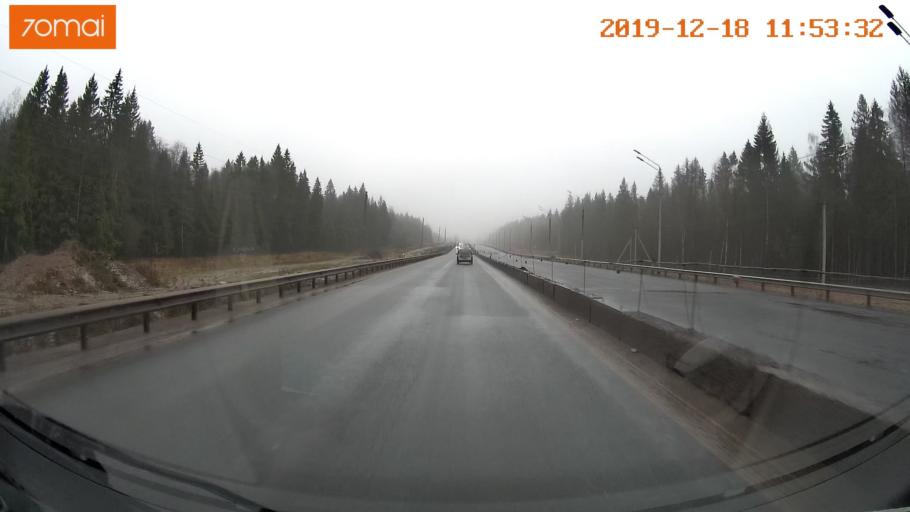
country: RU
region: Moskovskaya
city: Yershovo
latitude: 55.8054
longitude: 36.9198
